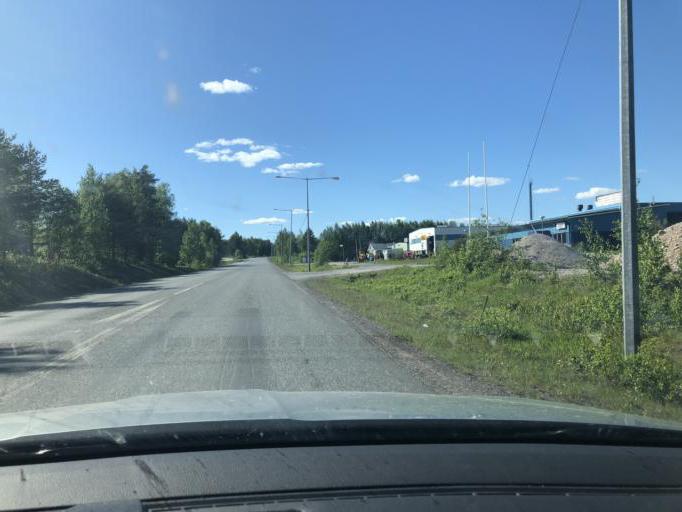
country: SE
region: Norrbotten
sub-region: Kalix Kommun
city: Kalix
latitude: 65.8581
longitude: 23.1694
